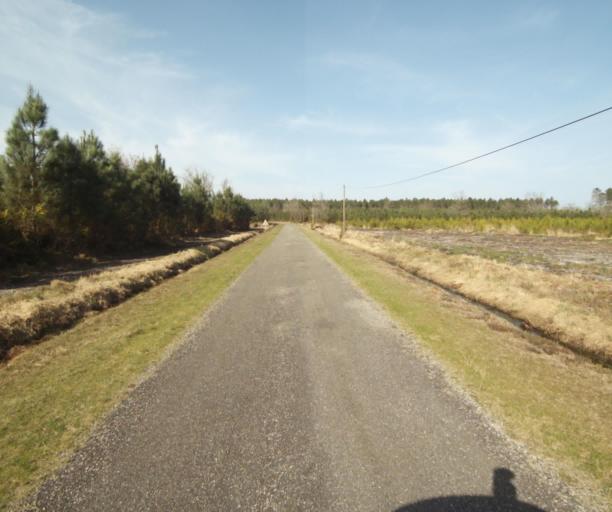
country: FR
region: Aquitaine
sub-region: Departement des Landes
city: Roquefort
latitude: 44.1380
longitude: -0.2012
